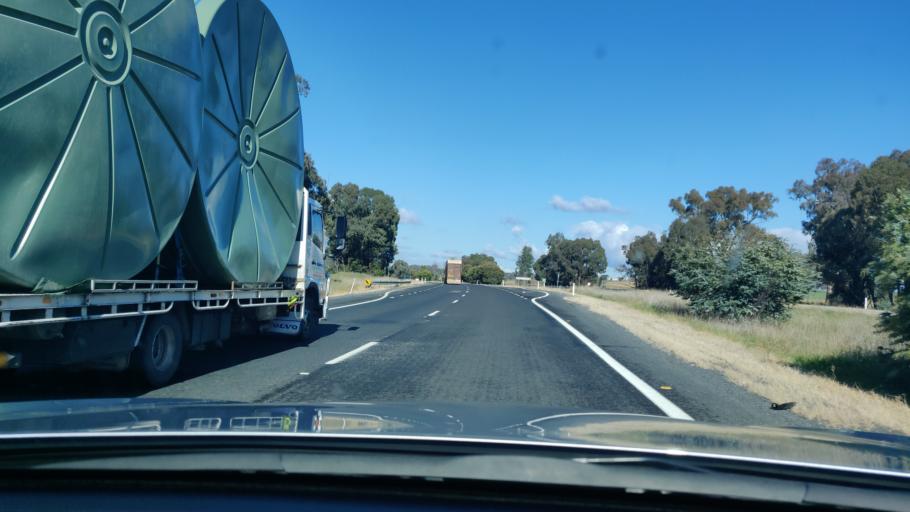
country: AU
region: New South Wales
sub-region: Wagga Wagga
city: Forest Hill
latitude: -35.3256
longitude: 147.6469
